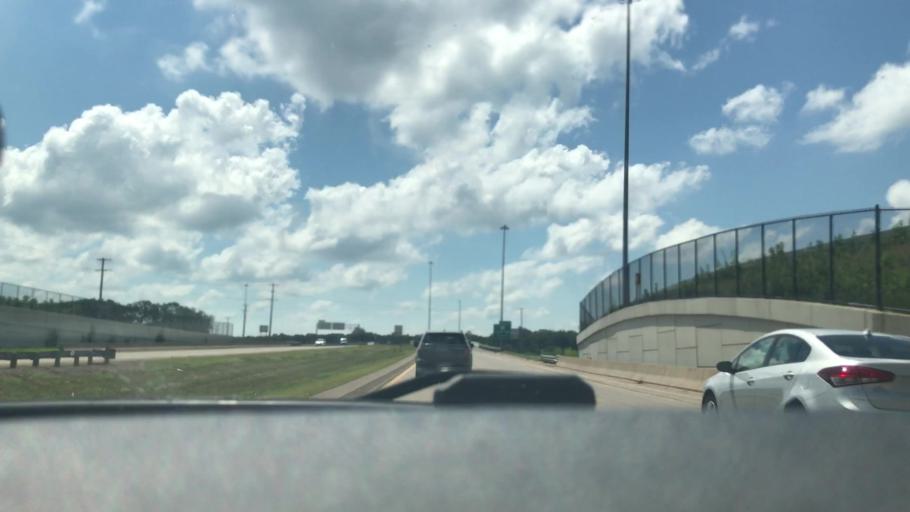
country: US
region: Wisconsin
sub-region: Eau Claire County
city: Altoona
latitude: 44.7894
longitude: -91.4536
